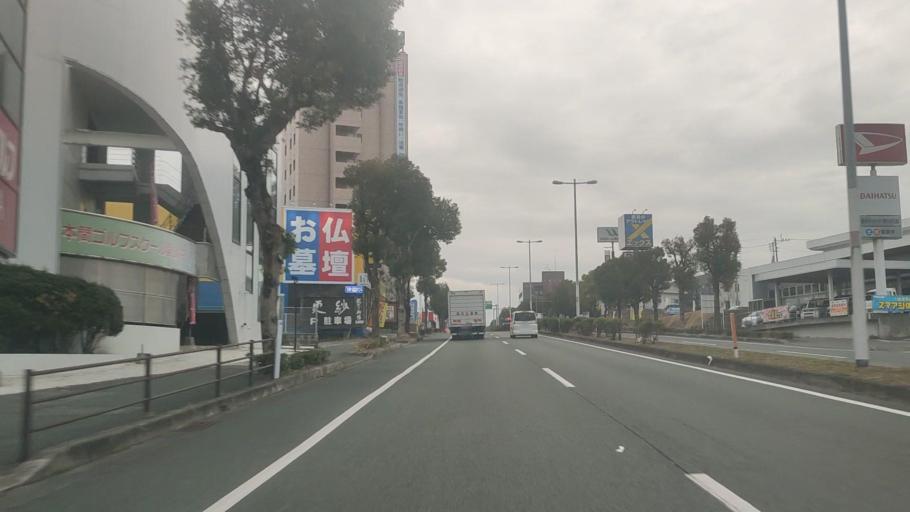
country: JP
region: Kumamoto
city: Kumamoto
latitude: 32.8212
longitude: 130.7588
